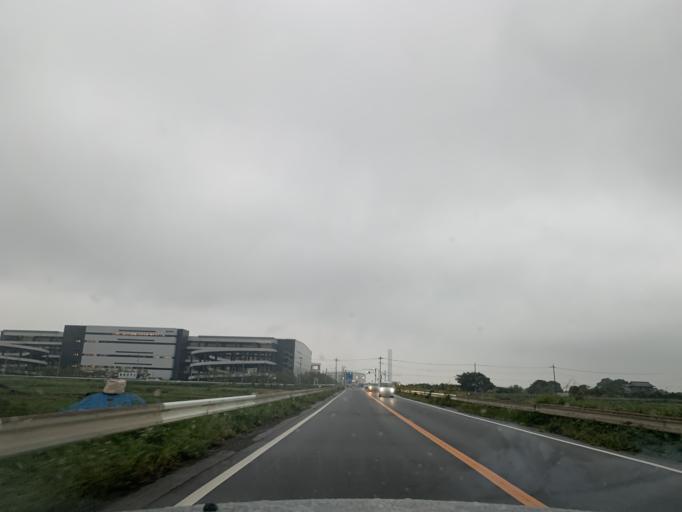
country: JP
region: Chiba
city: Nagareyama
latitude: 35.8903
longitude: 139.8949
